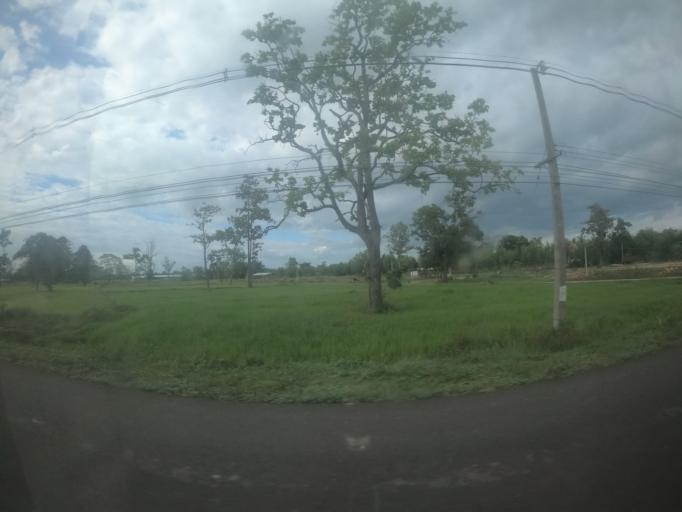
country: TH
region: Surin
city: Kap Choeng
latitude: 14.5558
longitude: 103.5041
